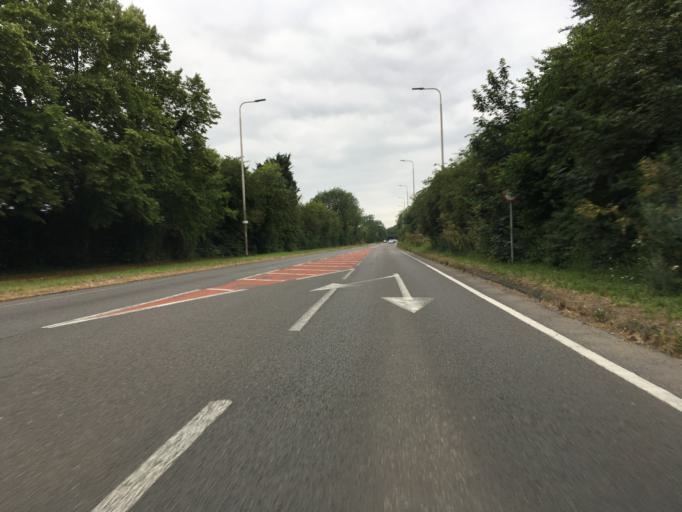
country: GB
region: England
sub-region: Hertfordshire
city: Markyate
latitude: 51.8321
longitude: -0.4512
